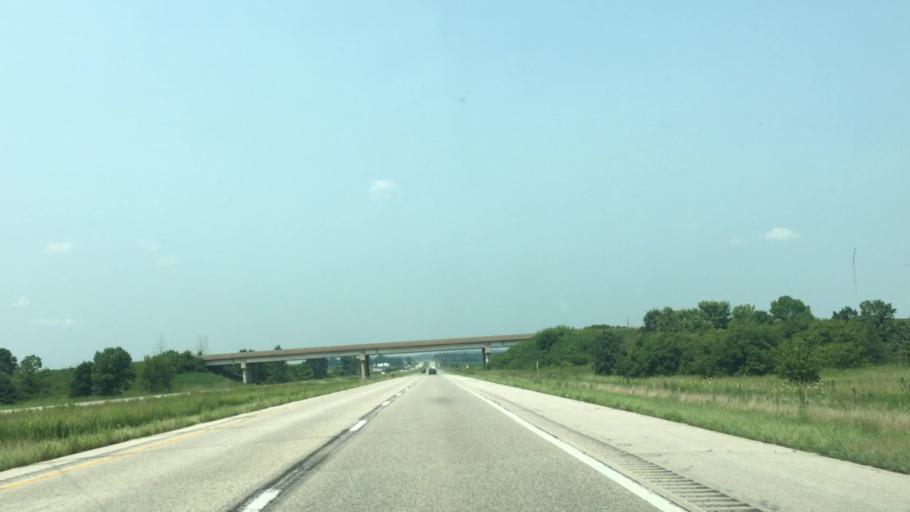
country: US
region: Iowa
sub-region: Linn County
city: Center Point
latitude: 42.1696
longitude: -91.7778
